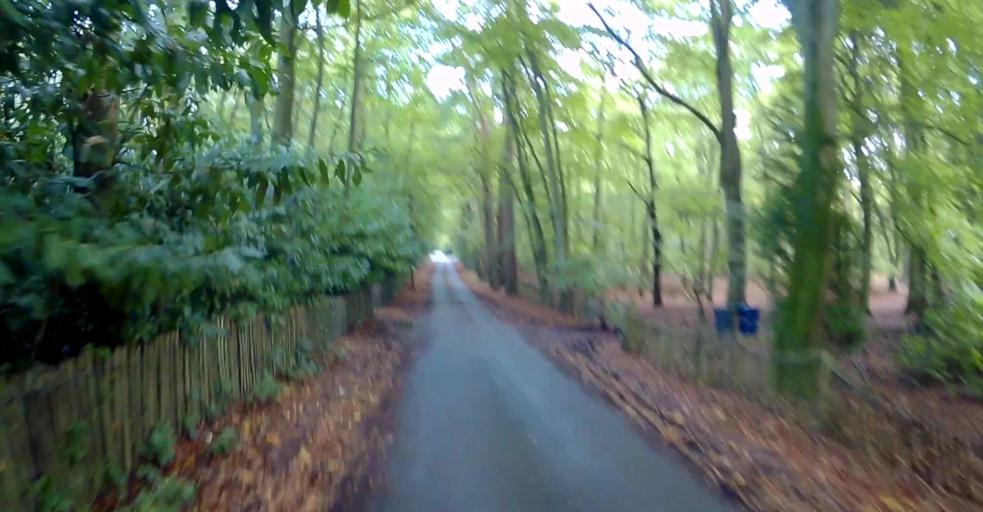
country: GB
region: England
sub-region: Surrey
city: Elstead
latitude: 51.1921
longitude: -0.7373
